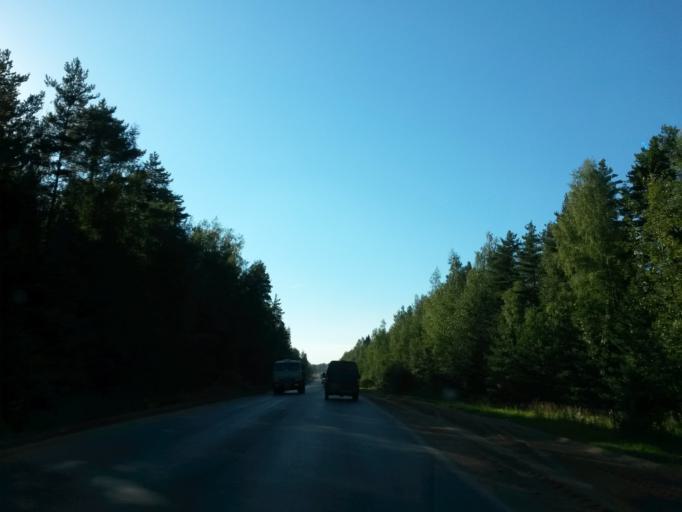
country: RU
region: Ivanovo
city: Novo-Talitsy
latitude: 57.0190
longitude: 40.7782
